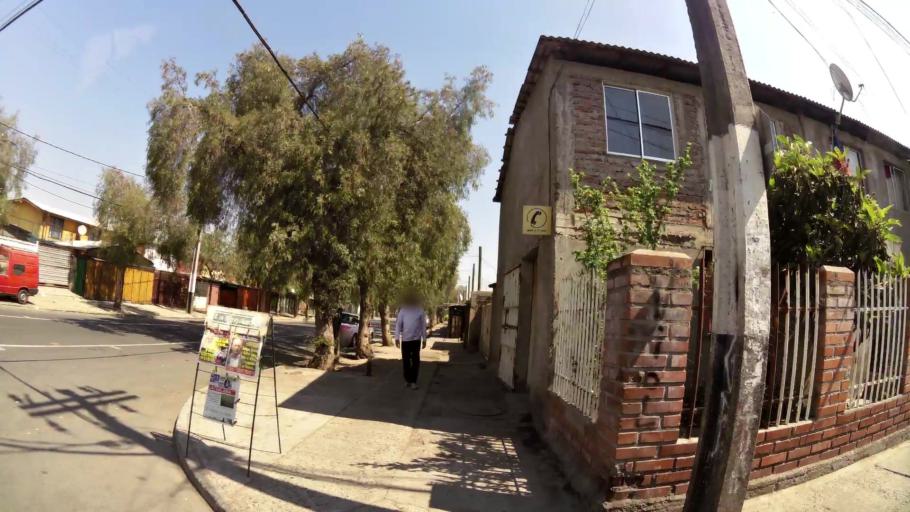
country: CL
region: Santiago Metropolitan
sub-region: Provincia de Santiago
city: La Pintana
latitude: -33.5601
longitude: -70.6132
